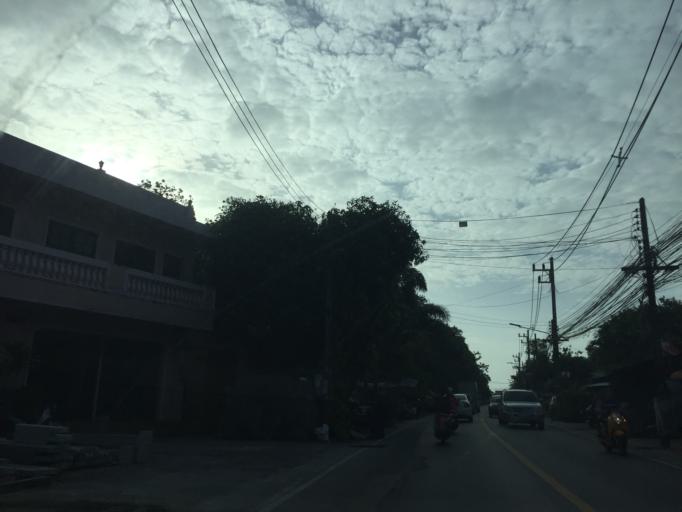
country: TH
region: Phuket
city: Mueang Phuket
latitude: 7.8620
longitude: 98.3713
